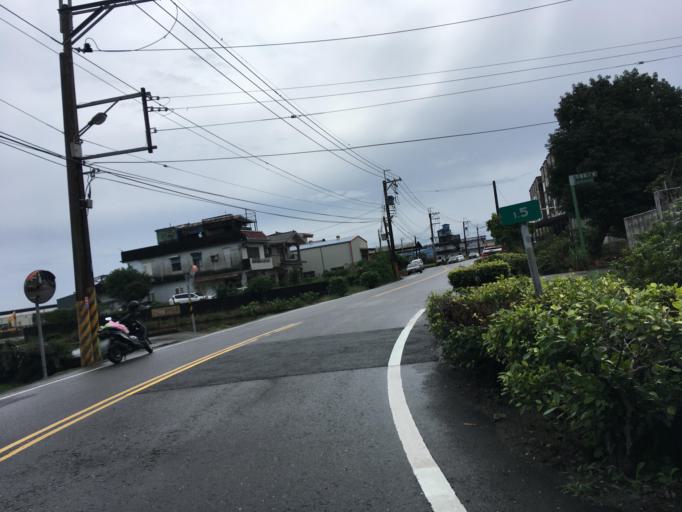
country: TW
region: Taiwan
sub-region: Yilan
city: Yilan
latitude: 24.6670
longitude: 121.7922
